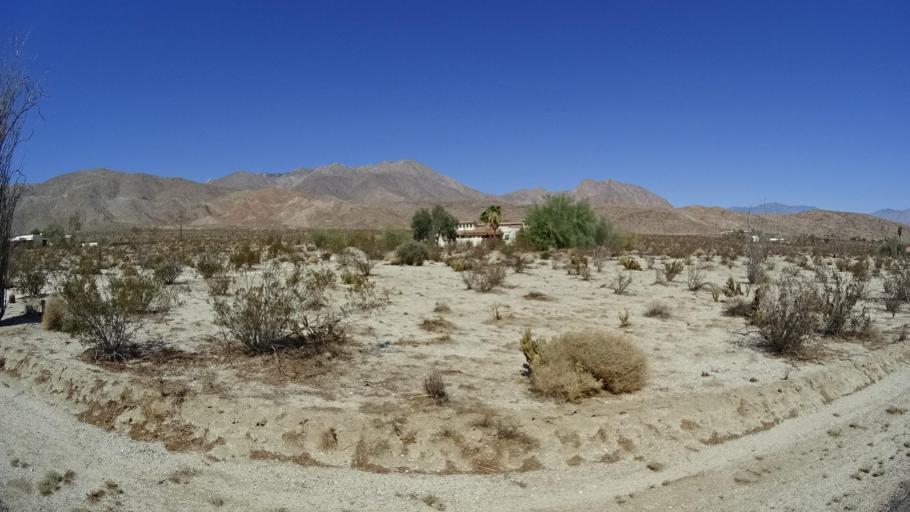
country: US
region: California
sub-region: San Diego County
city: Borrego Springs
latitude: 33.2331
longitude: -116.3869
